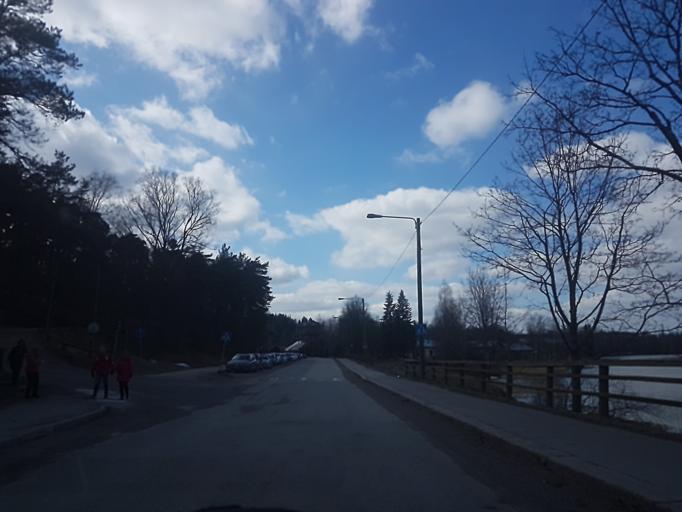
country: FI
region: Uusimaa
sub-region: Porvoo
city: Porvoo
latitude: 60.3964
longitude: 25.6536
